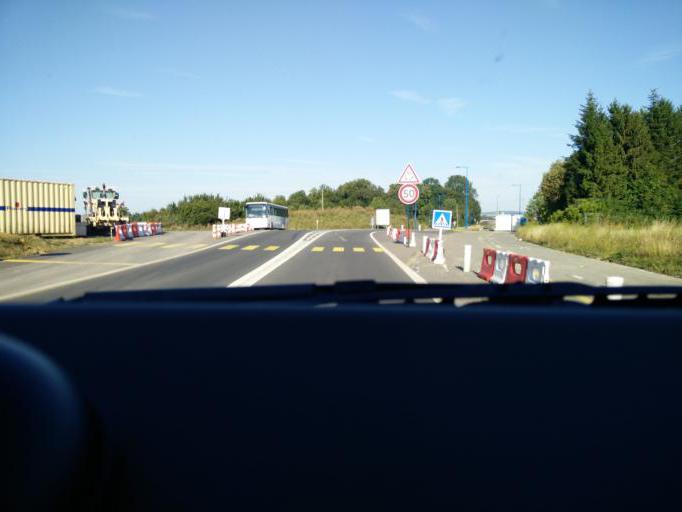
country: FR
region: Nord-Pas-de-Calais
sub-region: Departement du Pas-de-Calais
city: Houdain
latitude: 50.4524
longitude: 2.5467
